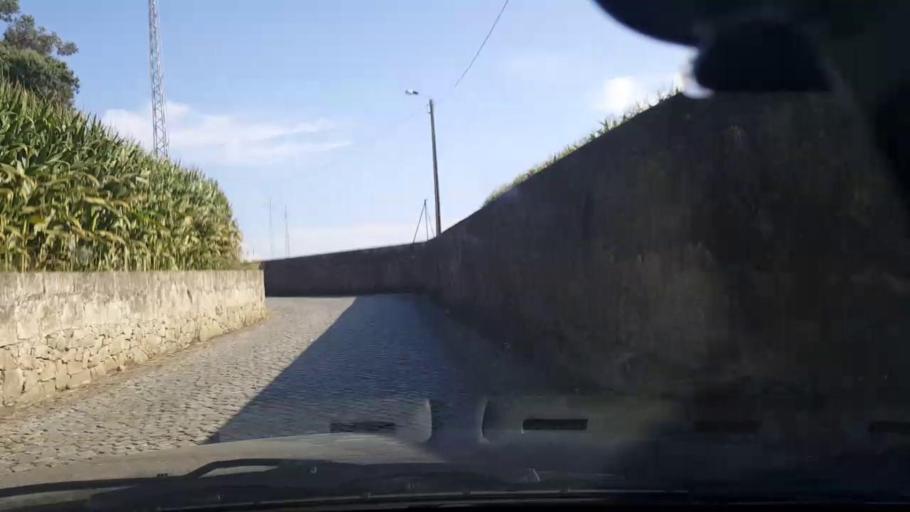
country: PT
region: Porto
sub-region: Maia
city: Gemunde
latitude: 41.2747
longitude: -8.6689
